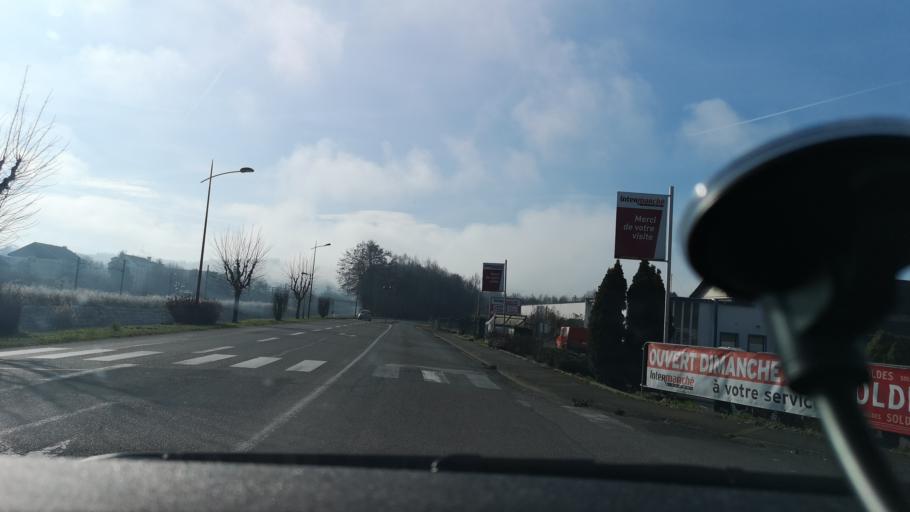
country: FR
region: Franche-Comte
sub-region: Departement du Doubs
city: Montenois
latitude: 47.4473
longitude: 6.5803
